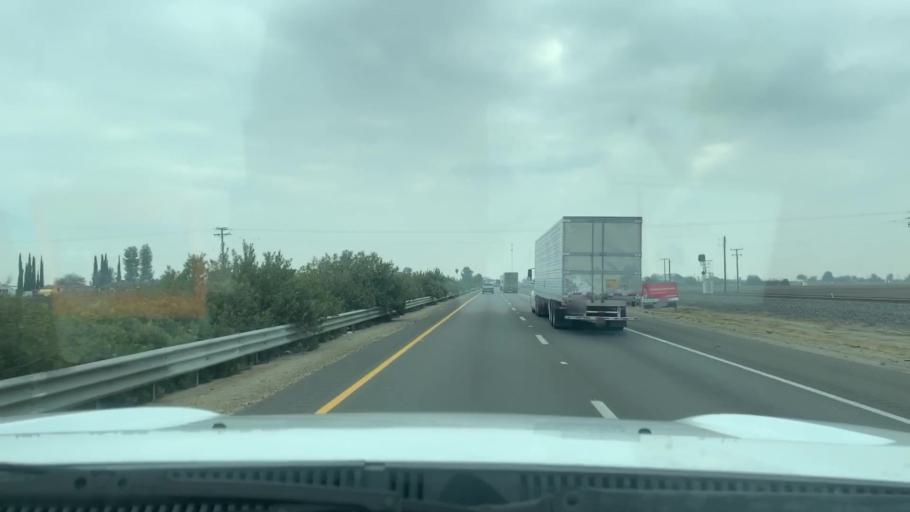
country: US
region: California
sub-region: Tulare County
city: Tipton
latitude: 36.0776
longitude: -119.3186
